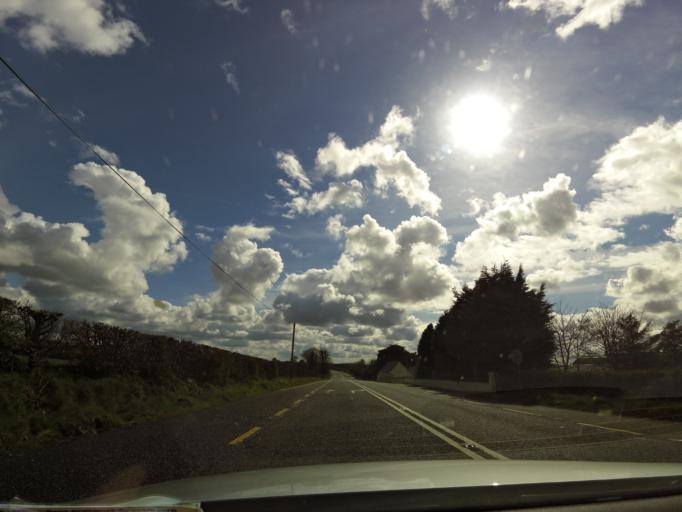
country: IE
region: Leinster
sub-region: Laois
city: Rathdowney
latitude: 52.7780
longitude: -7.5331
